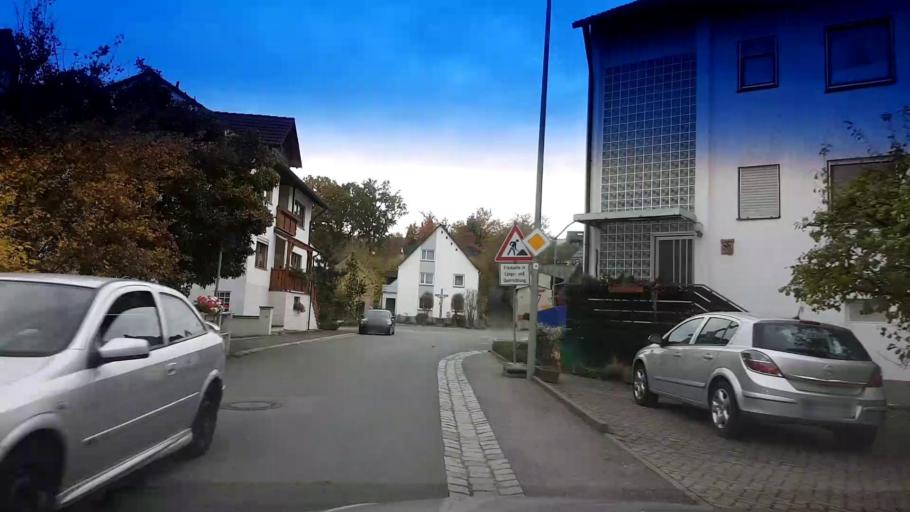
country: DE
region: Bavaria
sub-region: Upper Franconia
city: Viereth-Trunstadt
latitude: 49.9211
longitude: 10.7763
